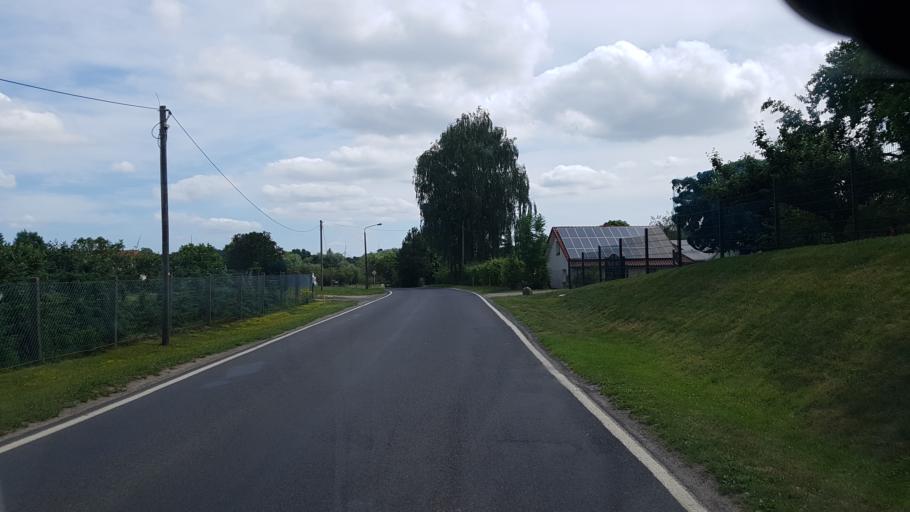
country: DE
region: Mecklenburg-Vorpommern
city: Strasburg
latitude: 53.4111
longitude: 13.7619
